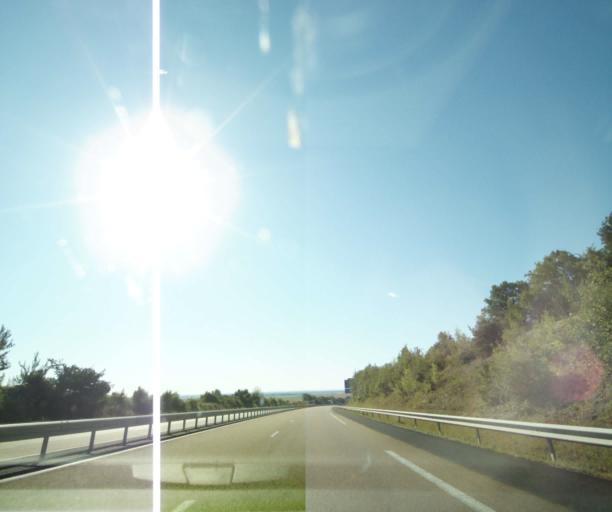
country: FR
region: Champagne-Ardenne
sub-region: Departement de l'Aube
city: La Riviere-de-Corps
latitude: 48.2703
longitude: 3.9562
